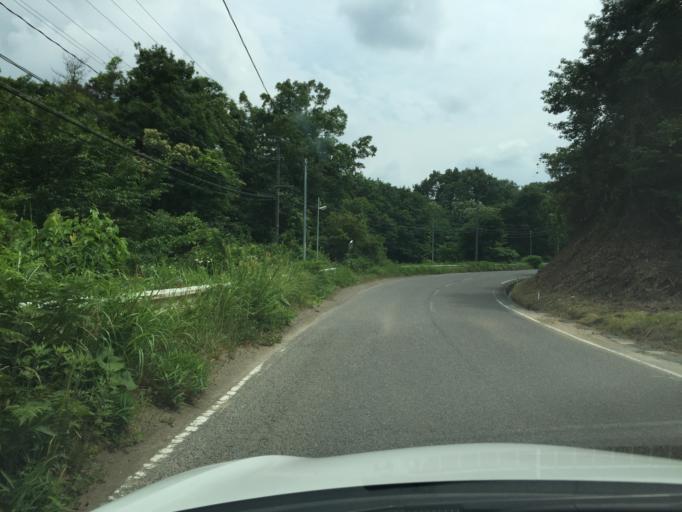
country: JP
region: Fukushima
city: Ishikawa
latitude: 37.2076
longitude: 140.4827
